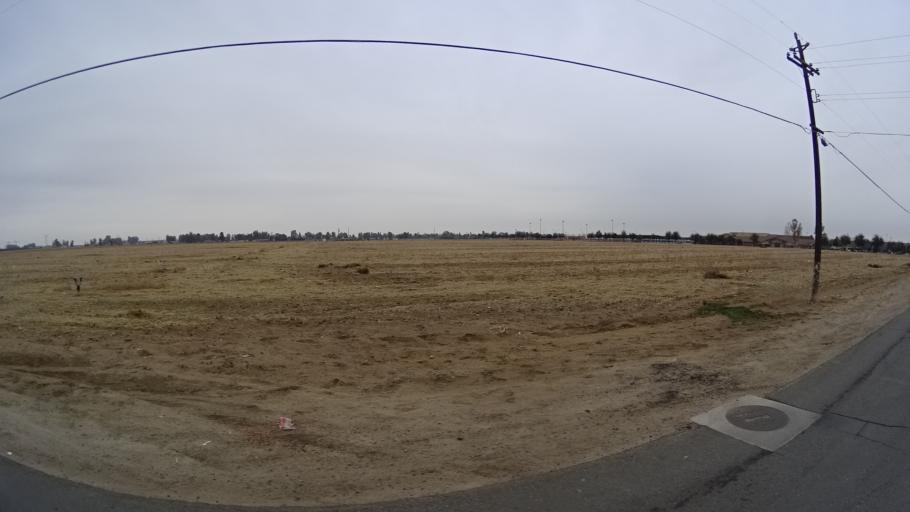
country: US
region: California
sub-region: Kern County
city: Lamont
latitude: 35.3399
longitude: -118.9294
